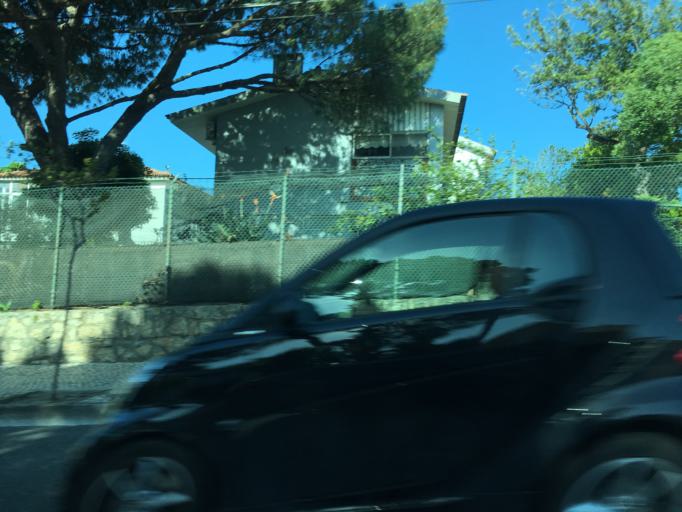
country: PT
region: Lisbon
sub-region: Cascais
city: Monte Estoril
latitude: 38.7093
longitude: -9.4180
